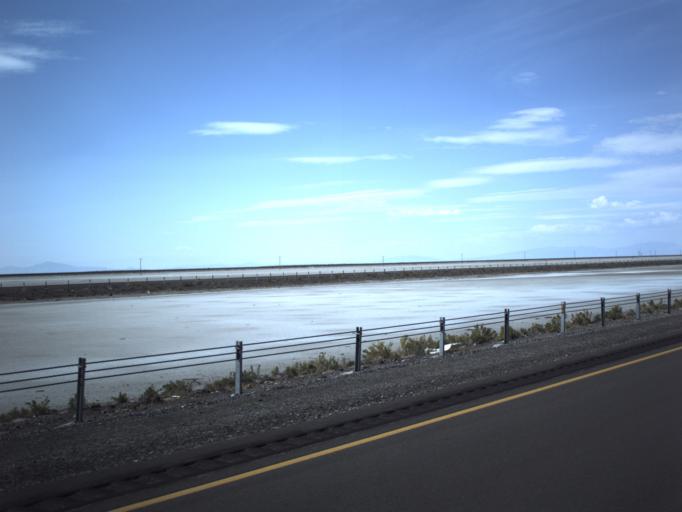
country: US
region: Utah
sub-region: Tooele County
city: Wendover
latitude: 40.7289
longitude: -113.3727
